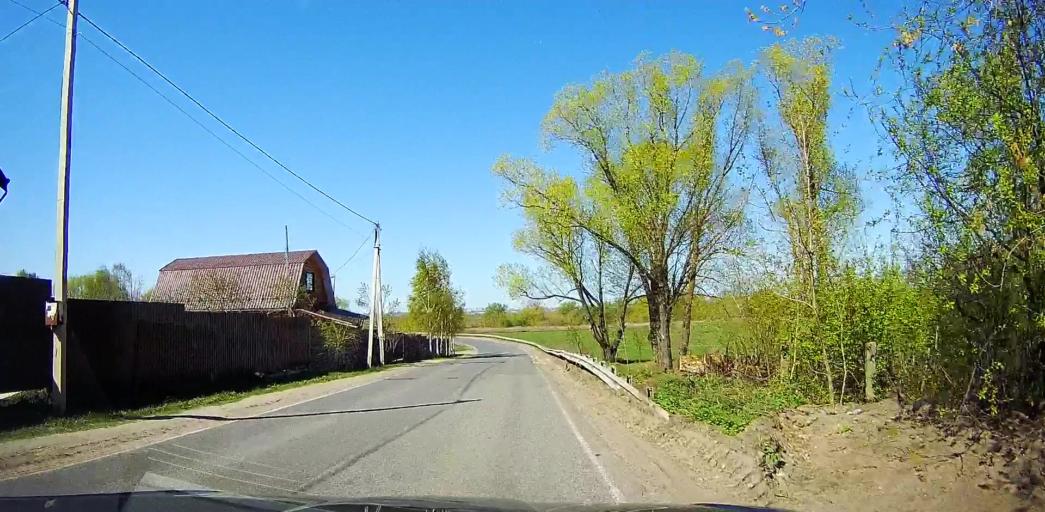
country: RU
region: Moskovskaya
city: Bronnitsy
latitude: 55.4906
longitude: 38.2381
